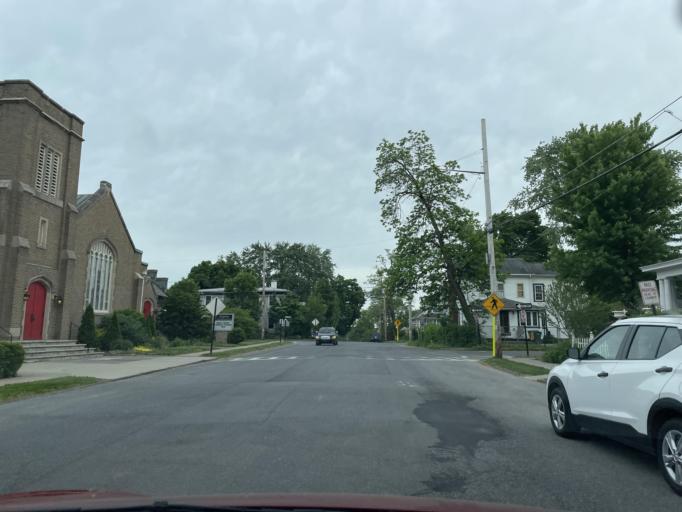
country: US
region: New York
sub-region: Ulster County
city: Saugerties
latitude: 42.0771
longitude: -73.9492
